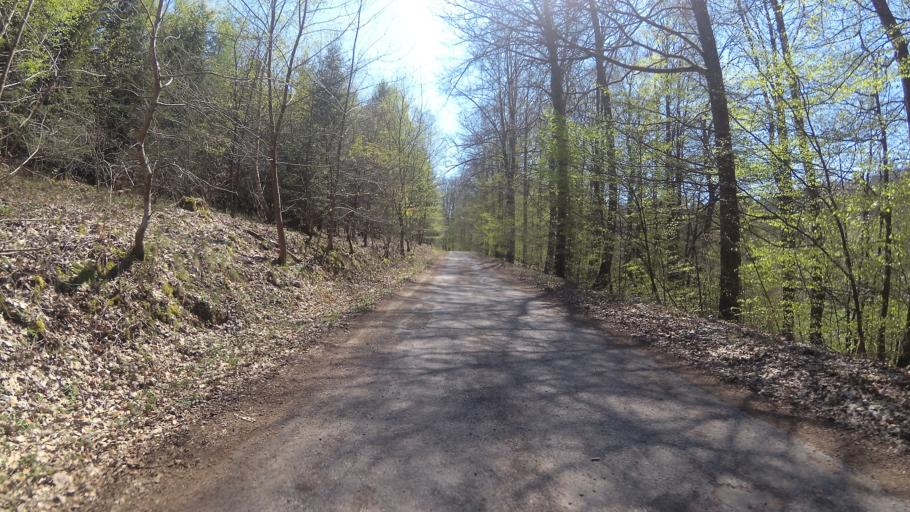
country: DE
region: Rheinland-Pfalz
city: Breitenbach
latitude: 49.4105
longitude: 7.2785
